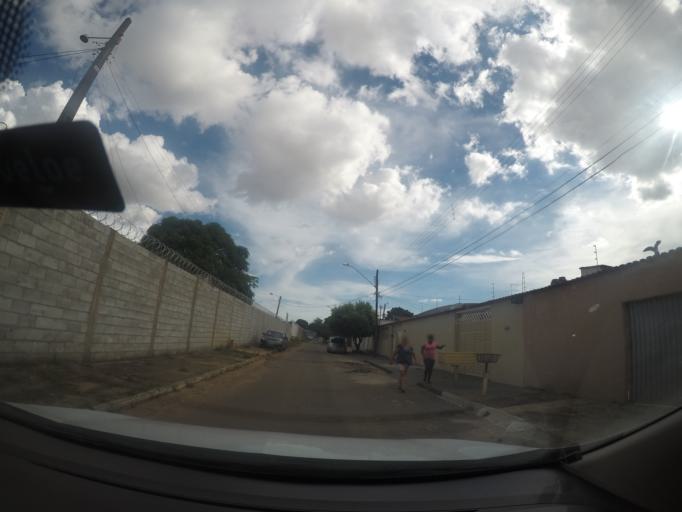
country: BR
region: Goias
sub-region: Goiania
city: Goiania
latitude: -16.6774
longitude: -49.3038
